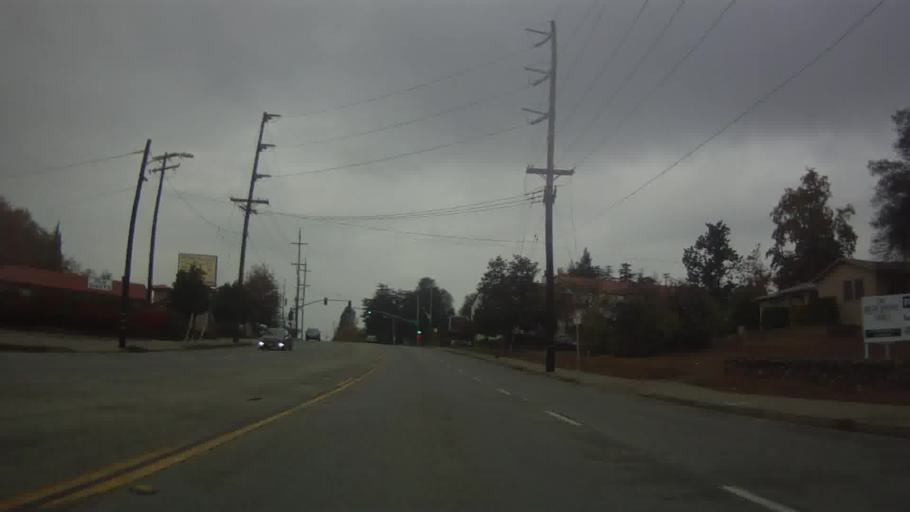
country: US
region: California
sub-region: Shasta County
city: Redding
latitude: 40.5866
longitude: -122.4019
